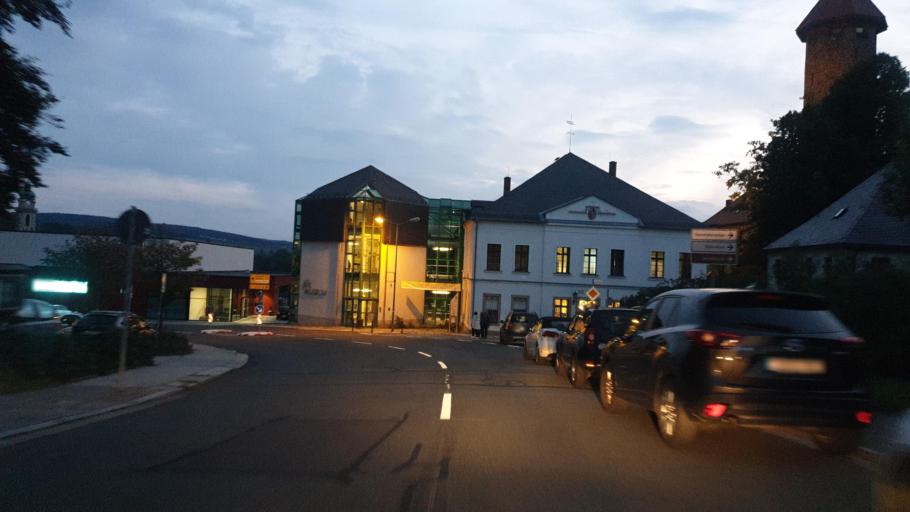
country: DE
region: Saxony
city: Auerbach
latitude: 50.5086
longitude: 12.4025
